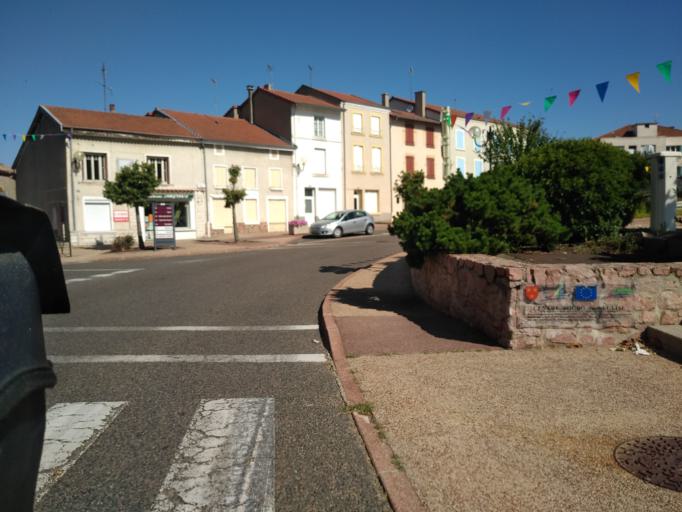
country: FR
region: Rhone-Alpes
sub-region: Departement de la Loire
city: Neulise
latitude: 45.9025
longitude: 4.1803
